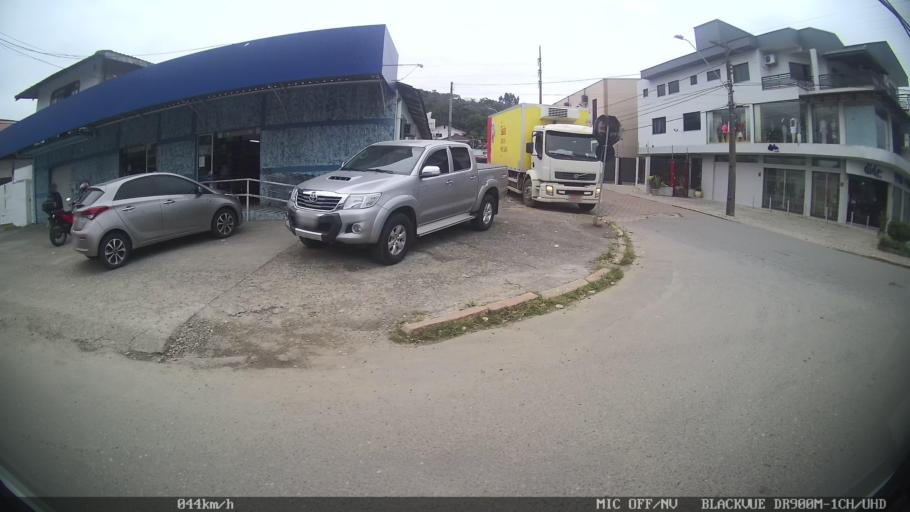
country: BR
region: Santa Catarina
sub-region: Joinville
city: Joinville
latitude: -26.2962
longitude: -48.8181
